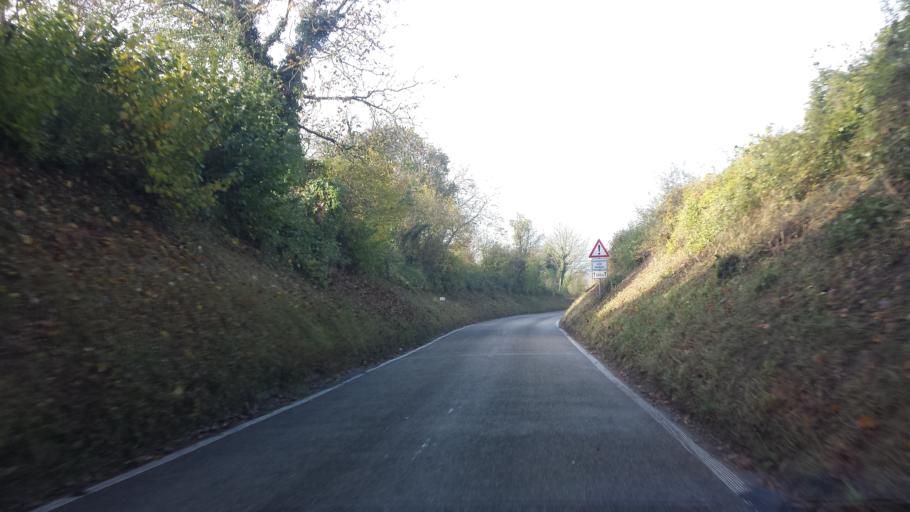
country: DE
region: Baden-Wuerttemberg
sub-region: Karlsruhe Region
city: Gondelsheim
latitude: 49.1026
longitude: 8.6616
